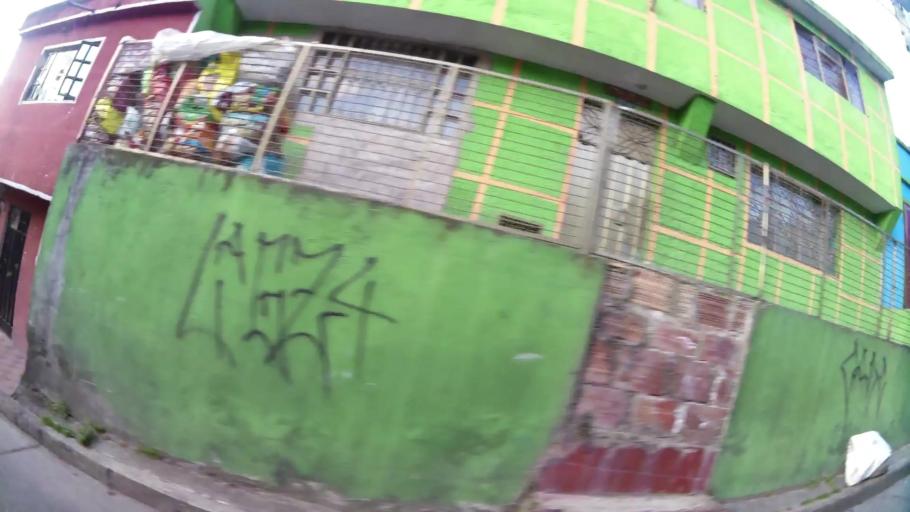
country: CO
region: Bogota D.C.
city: Bogota
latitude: 4.5415
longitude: -74.0851
